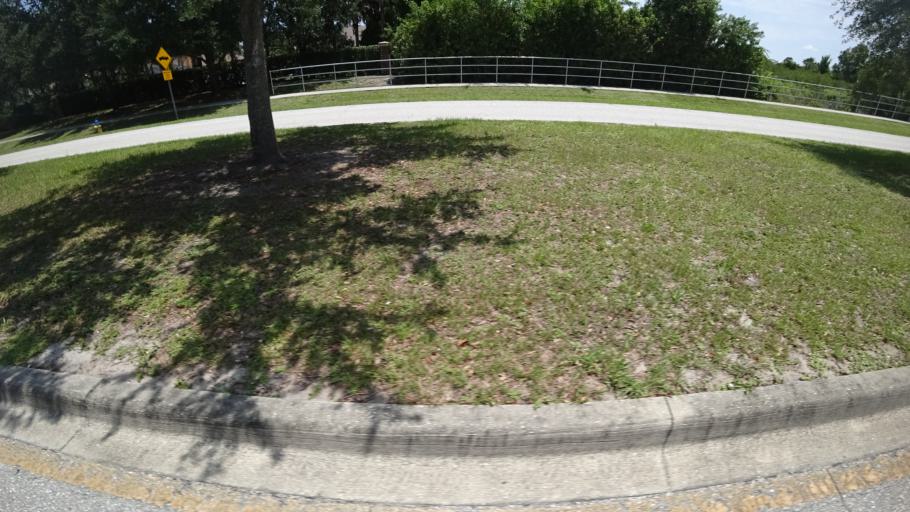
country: US
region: Florida
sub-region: Sarasota County
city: Desoto Lakes
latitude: 27.4087
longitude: -82.4629
